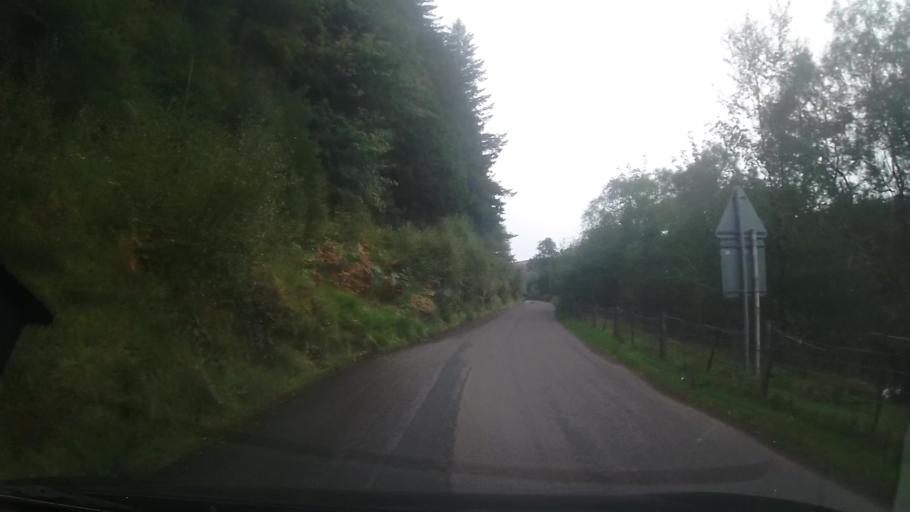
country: GB
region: Wales
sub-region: Sir Powys
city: Rhayader
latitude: 52.2933
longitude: -3.5985
